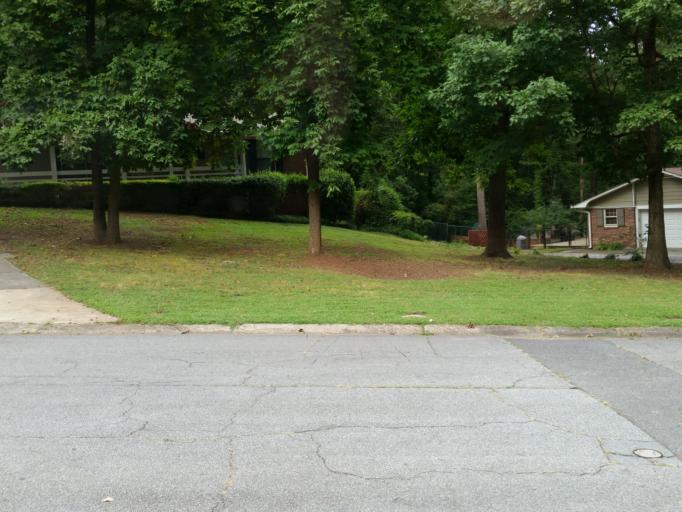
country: US
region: Georgia
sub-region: Cobb County
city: Marietta
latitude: 34.0194
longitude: -84.5466
